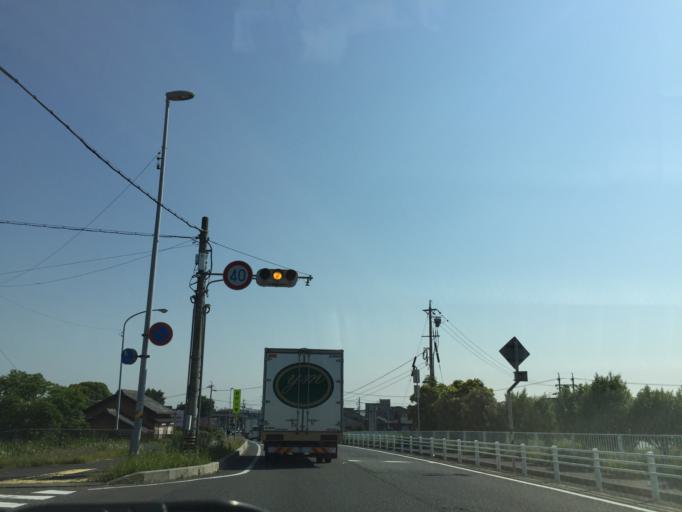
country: JP
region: Mie
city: Yokkaichi
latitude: 35.0457
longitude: 136.6775
